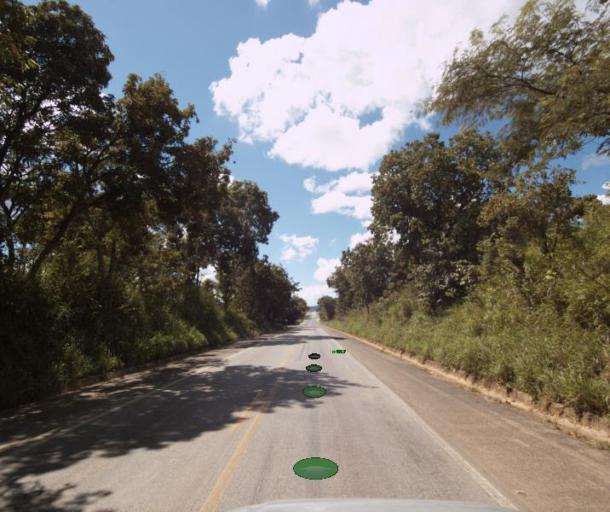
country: BR
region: Goias
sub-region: Porangatu
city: Porangatu
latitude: -13.7191
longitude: -49.0212
